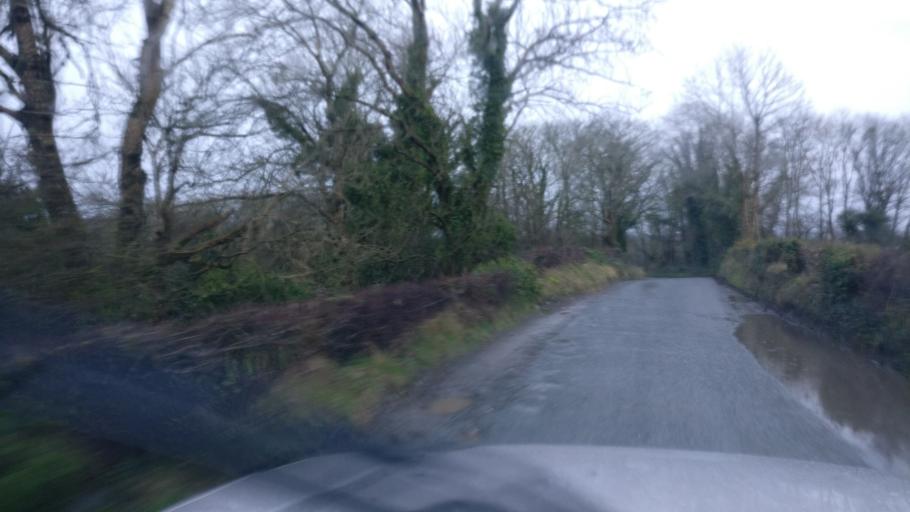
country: IE
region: Connaught
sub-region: County Galway
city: Ballinasloe
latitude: 53.3004
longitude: -8.2720
